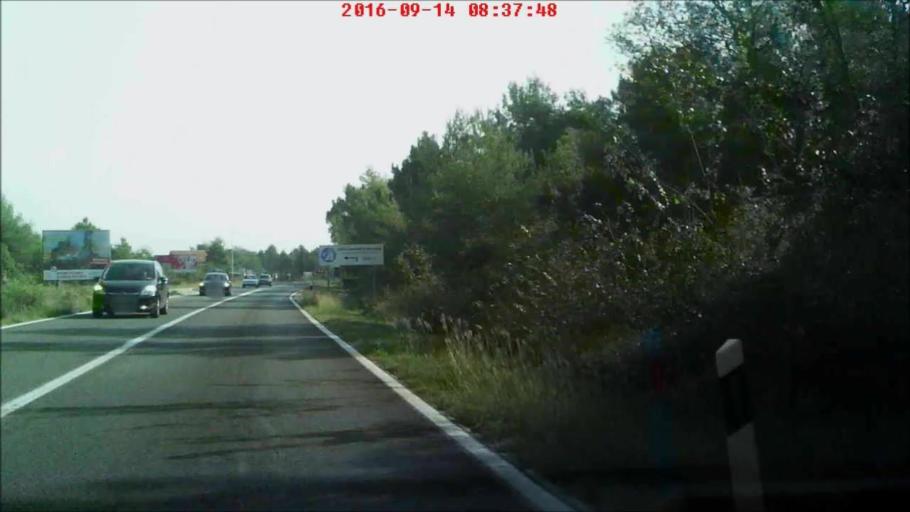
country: HR
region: Zadarska
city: Policnik
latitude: 44.1674
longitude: 15.3570
